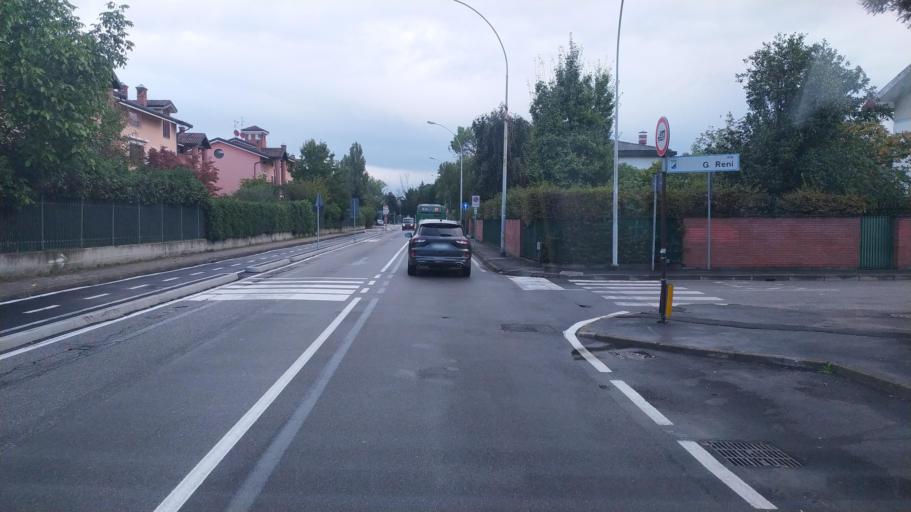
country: IT
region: Lombardy
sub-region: Citta metropolitana di Milano
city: Trezzano sul Naviglio
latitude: 45.4302
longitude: 9.0583
